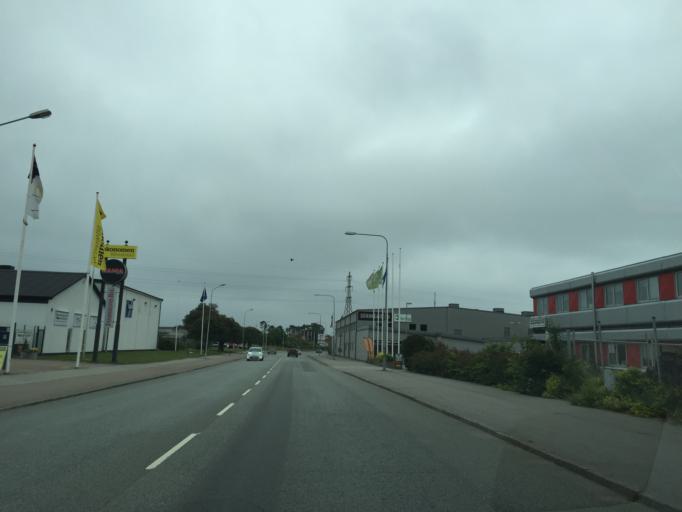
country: SE
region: Skane
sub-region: Ystads Kommun
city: Ystad
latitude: 55.4372
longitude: 13.8362
